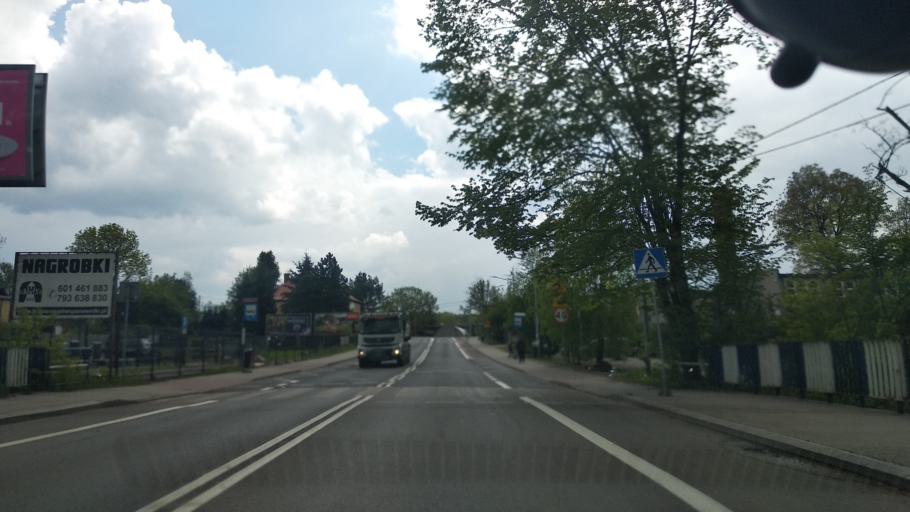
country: PL
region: Silesian Voivodeship
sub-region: Powiat mikolowski
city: Mikolow
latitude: 50.2293
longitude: 18.9165
